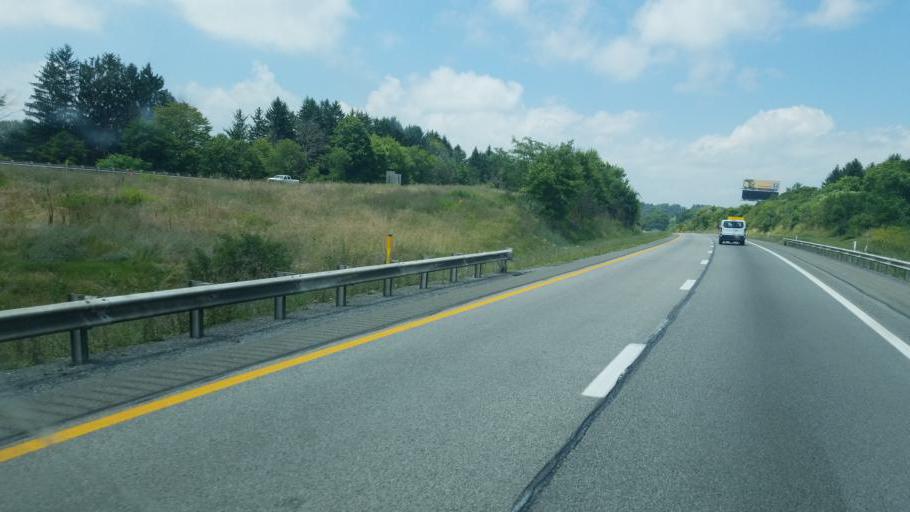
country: US
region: West Virginia
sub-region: Mercer County
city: Athens
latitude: 37.3820
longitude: -81.0459
